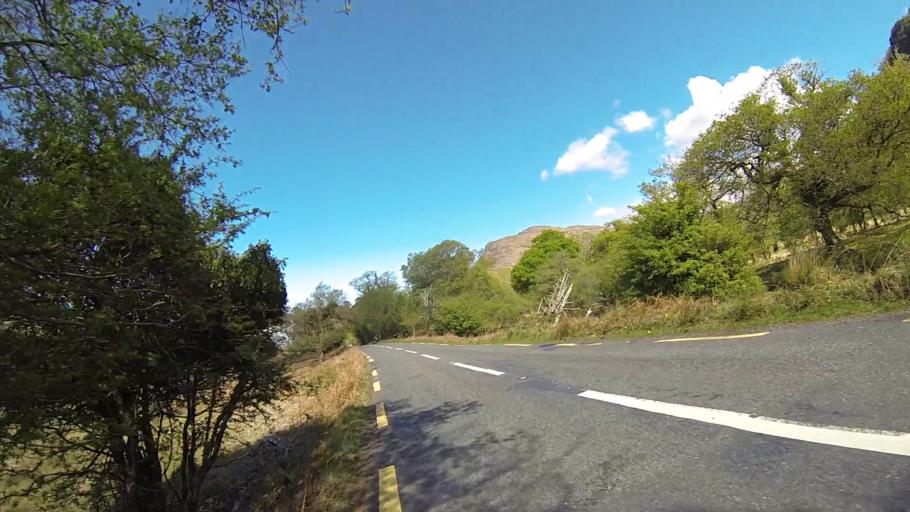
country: IE
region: Munster
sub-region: Ciarrai
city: Cill Airne
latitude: 51.9860
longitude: -9.5603
